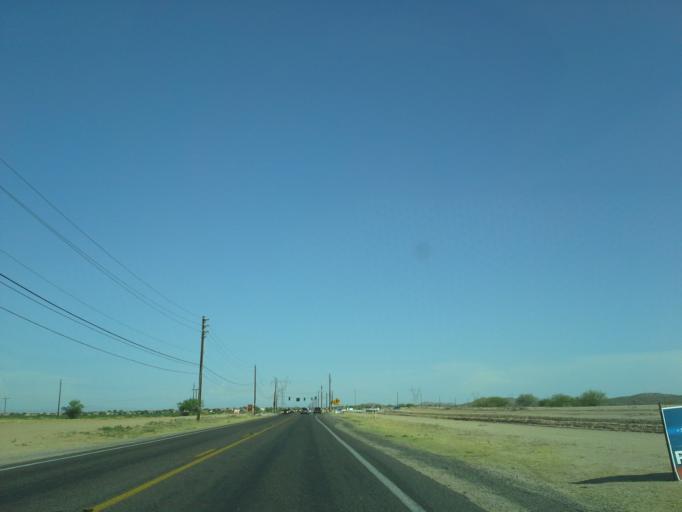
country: US
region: Arizona
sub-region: Pinal County
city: San Tan Valley
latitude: 33.1485
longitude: -111.5519
